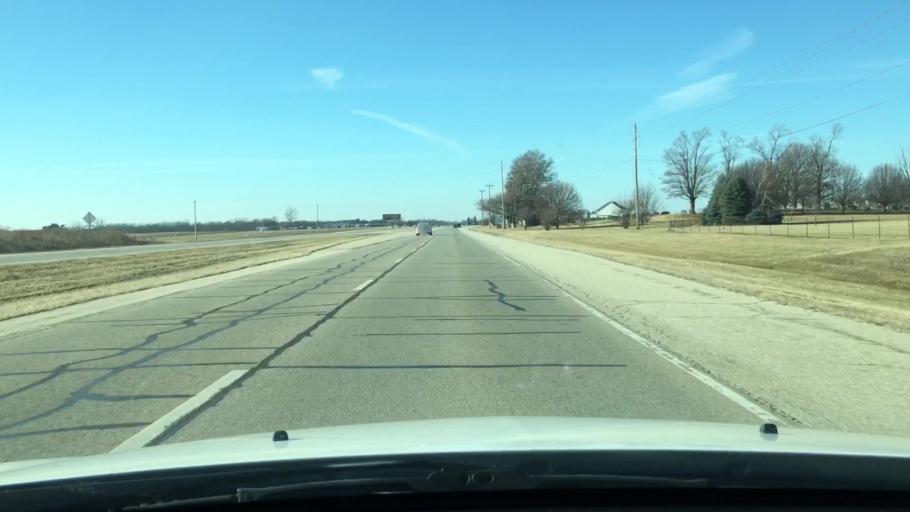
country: US
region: Illinois
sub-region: Woodford County
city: Germantown Hills
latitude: 40.7765
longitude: -89.4205
